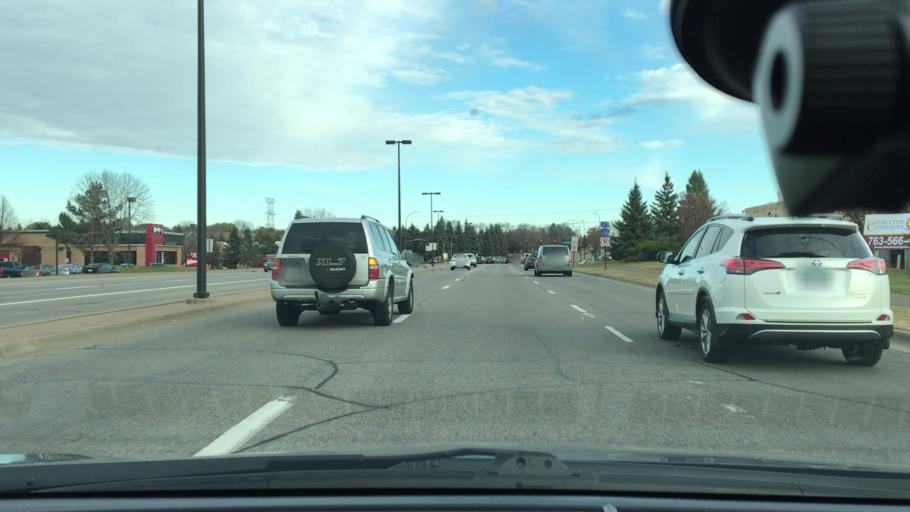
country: US
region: Minnesota
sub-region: Hennepin County
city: Maple Grove
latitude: 45.1049
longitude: -93.4547
